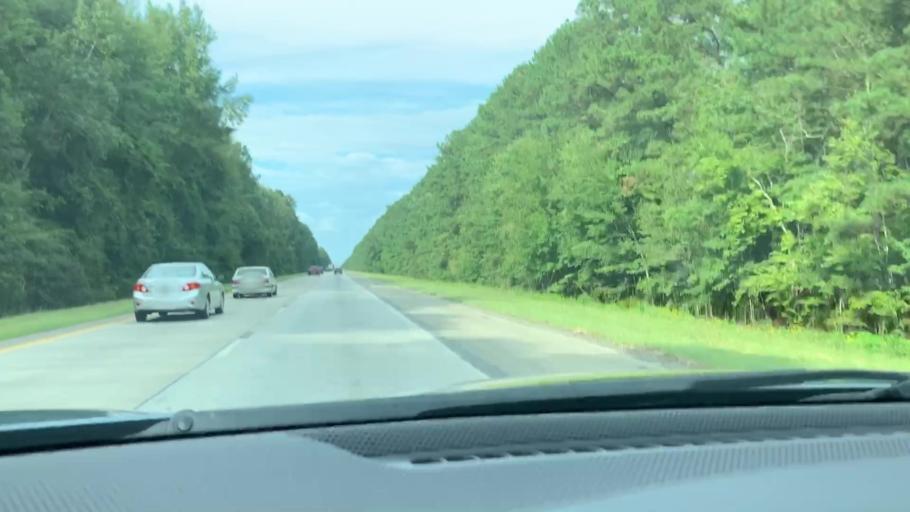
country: US
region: South Carolina
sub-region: Colleton County
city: Walterboro
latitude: 32.9700
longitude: -80.6761
